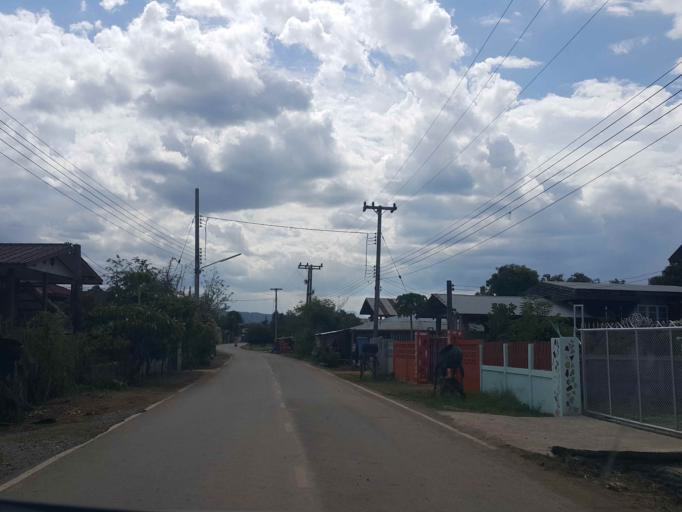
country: TH
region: Sukhothai
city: Thung Saliam
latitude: 17.3261
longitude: 99.4437
